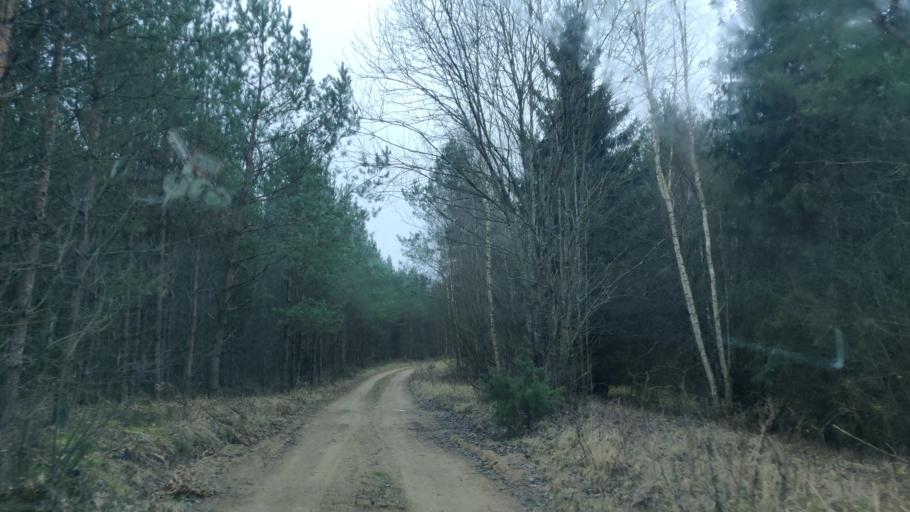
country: LT
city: Trakai
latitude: 54.5621
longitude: 24.9608
